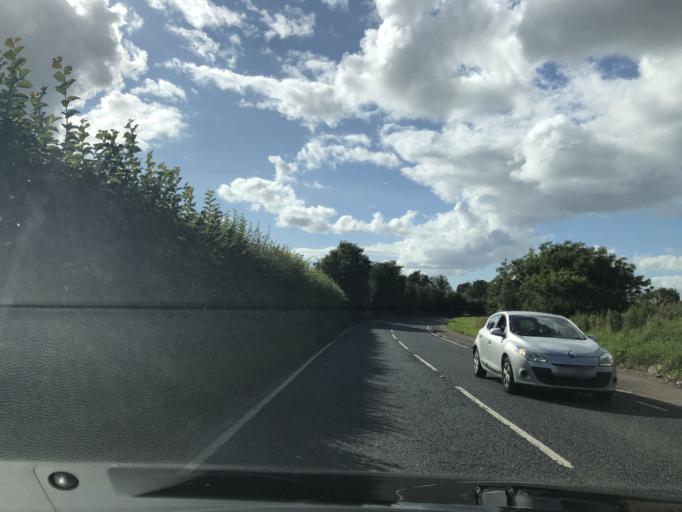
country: GB
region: Northern Ireland
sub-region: Castlereagh District
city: Dundonald
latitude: 54.5754
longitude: -5.7837
